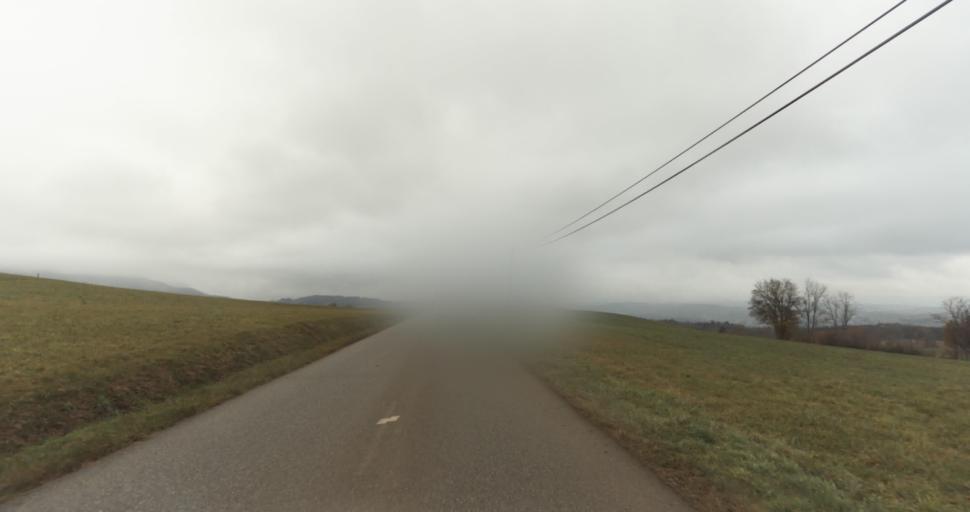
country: FR
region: Rhone-Alpes
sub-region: Departement de la Haute-Savoie
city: Thorens-Glieres
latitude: 46.0127
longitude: 6.2400
